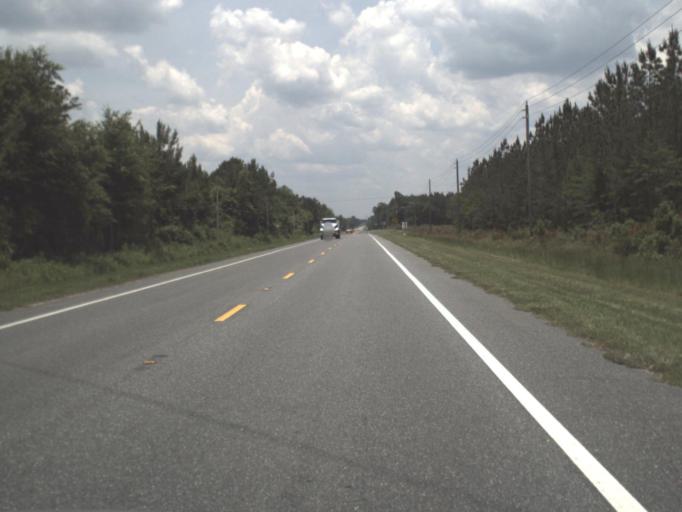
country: US
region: Florida
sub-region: Columbia County
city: Watertown
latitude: 30.1609
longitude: -82.5672
